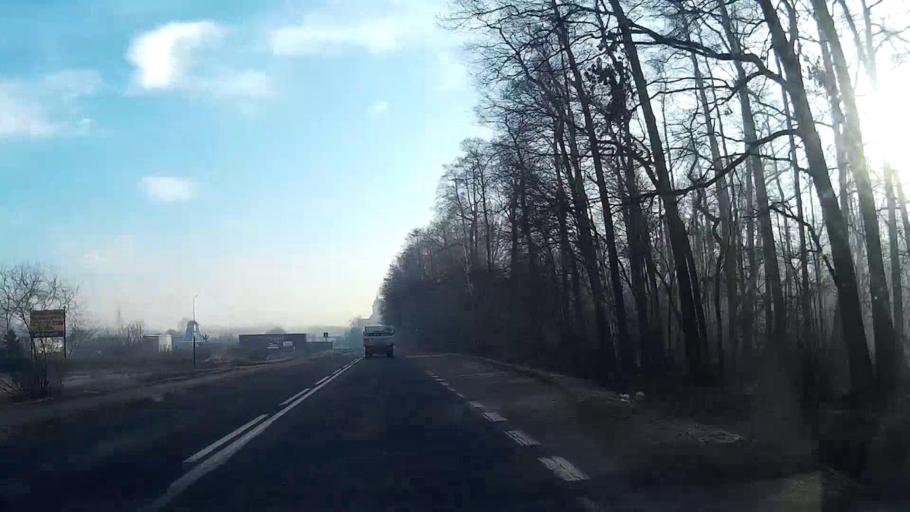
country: PL
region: Lesser Poland Voivodeship
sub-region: Powiat oswiecimski
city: Chelmek
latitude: 50.0715
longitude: 19.2554
